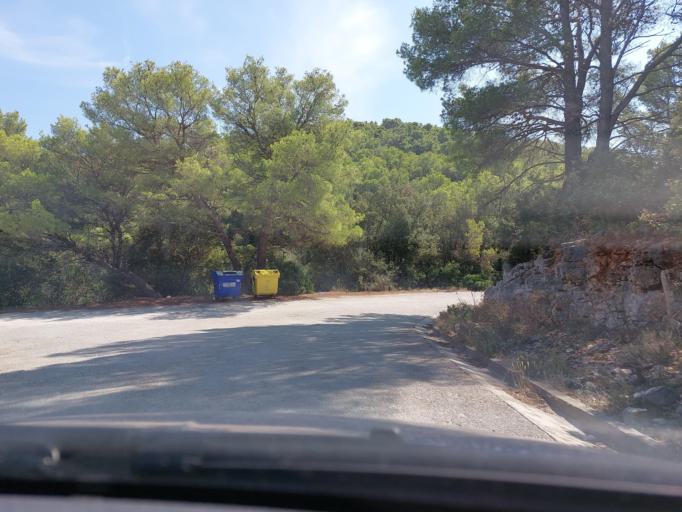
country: HR
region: Dubrovacko-Neretvanska
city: Smokvica
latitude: 42.7425
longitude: 16.8257
